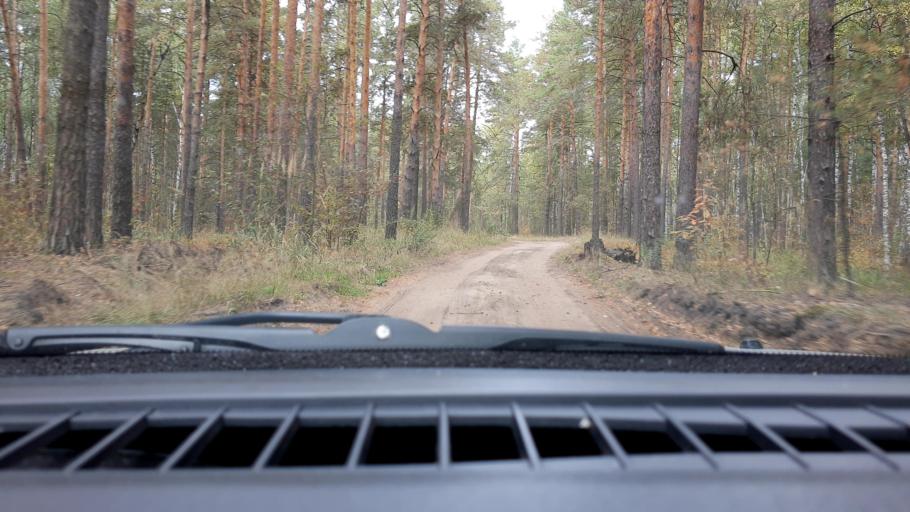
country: RU
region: Nizjnij Novgorod
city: Gorbatovka
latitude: 56.3226
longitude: 43.6919
